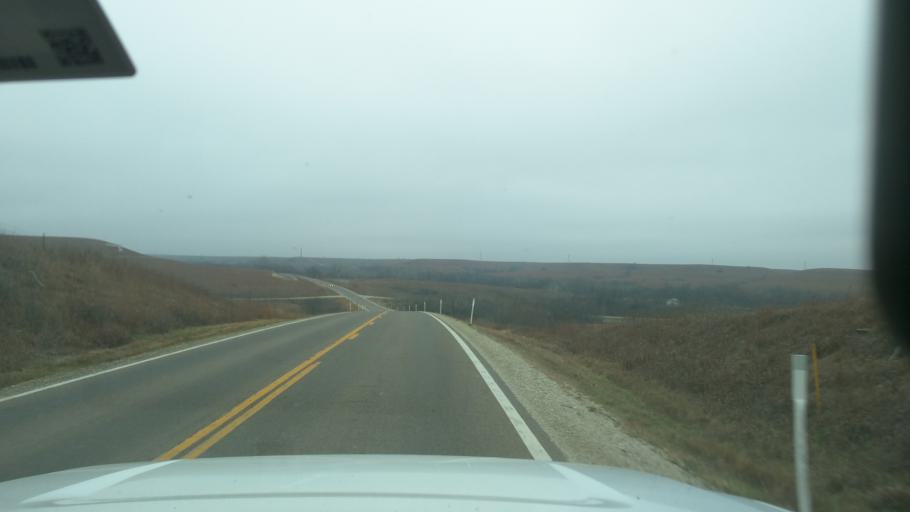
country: US
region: Kansas
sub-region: Riley County
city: Manhattan
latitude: 39.0193
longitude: -96.5386
